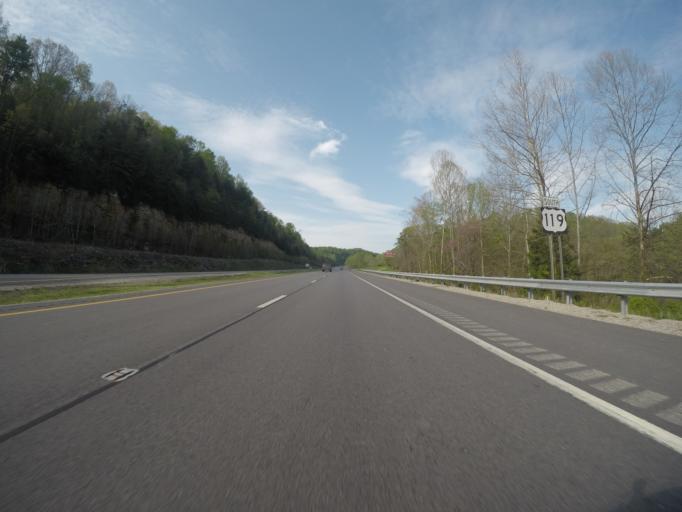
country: US
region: West Virginia
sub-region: Kanawha County
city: Dunbar
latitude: 38.3078
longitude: -81.7328
